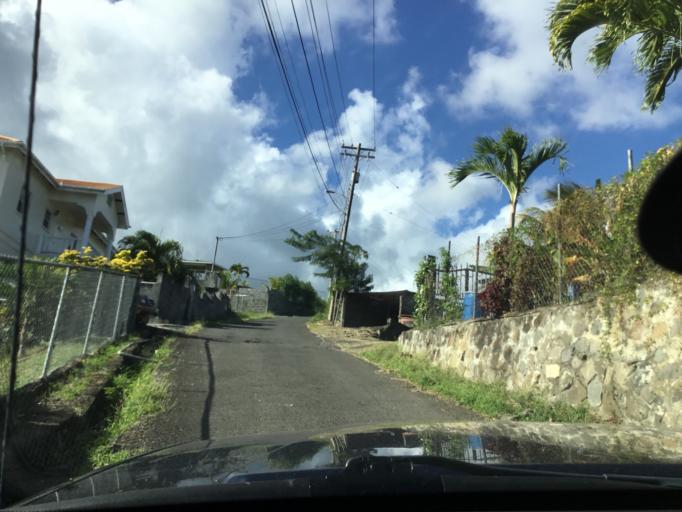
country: VC
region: Saint George
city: Kingstown
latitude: 13.1510
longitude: -61.1789
